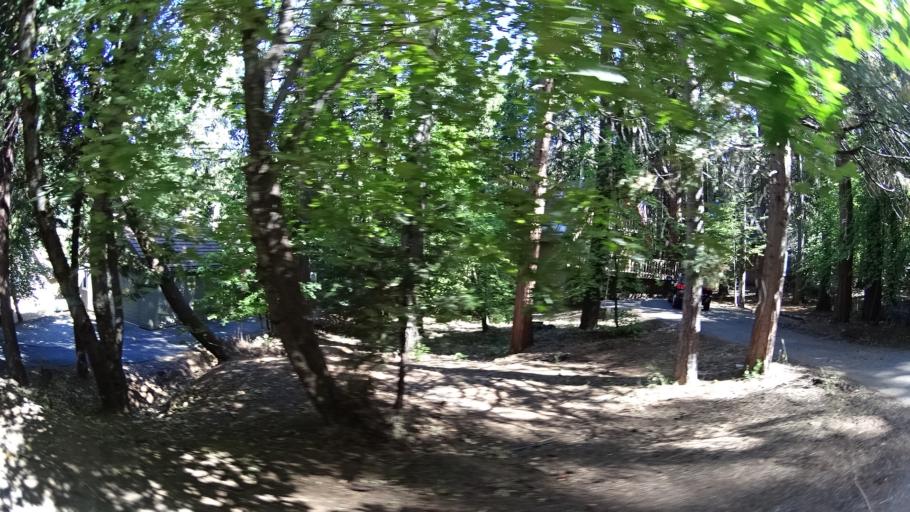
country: US
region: California
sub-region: Calaveras County
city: Arnold
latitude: 38.2537
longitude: -120.3218
